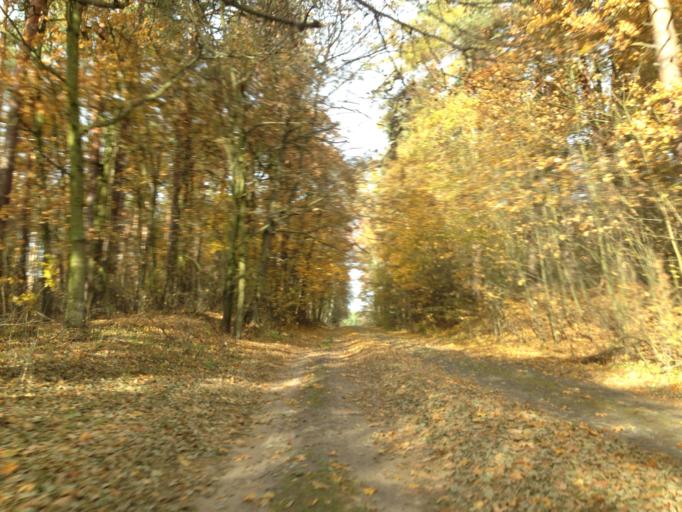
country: PL
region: Kujawsko-Pomorskie
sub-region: Powiat brodnicki
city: Gorzno
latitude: 53.2274
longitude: 19.6559
